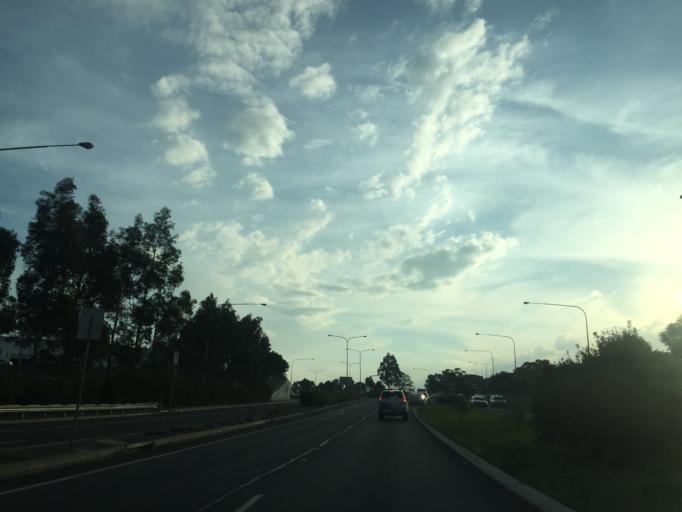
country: AU
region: New South Wales
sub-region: Blacktown
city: Stanhope Gardens
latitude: -33.7212
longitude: 150.9343
